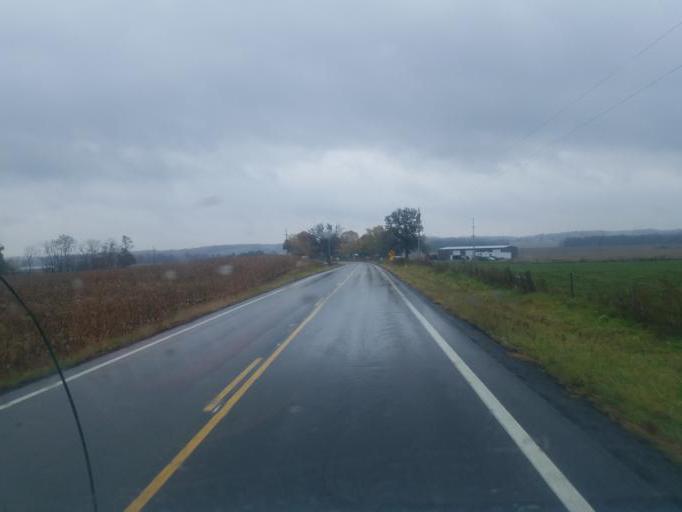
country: US
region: Ohio
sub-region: Knox County
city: Gambier
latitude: 40.3181
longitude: -82.4074
